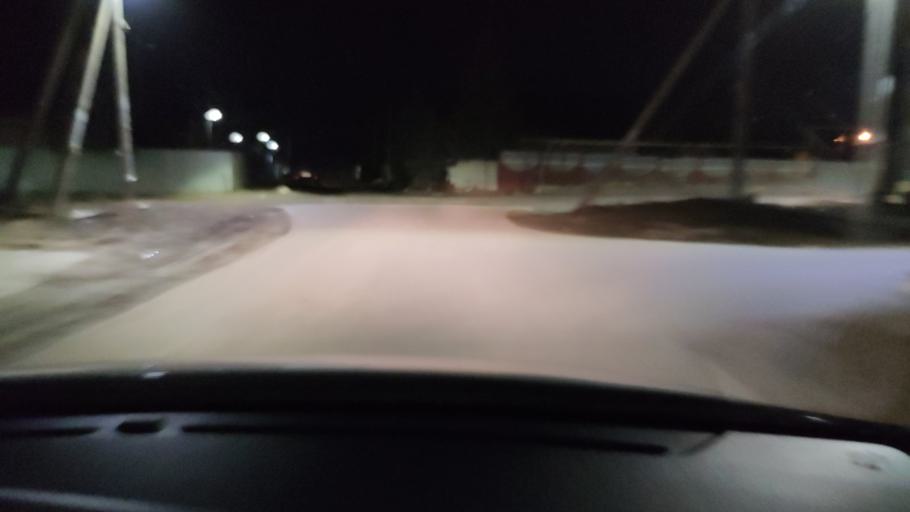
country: RU
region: Tatarstan
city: Vysokaya Gora
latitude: 55.8532
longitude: 49.2377
